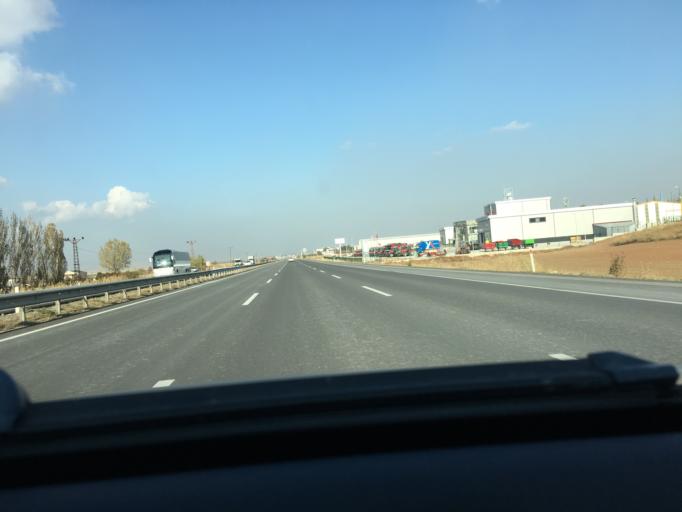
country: TR
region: Ankara
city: Polatli
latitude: 39.6393
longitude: 32.2039
